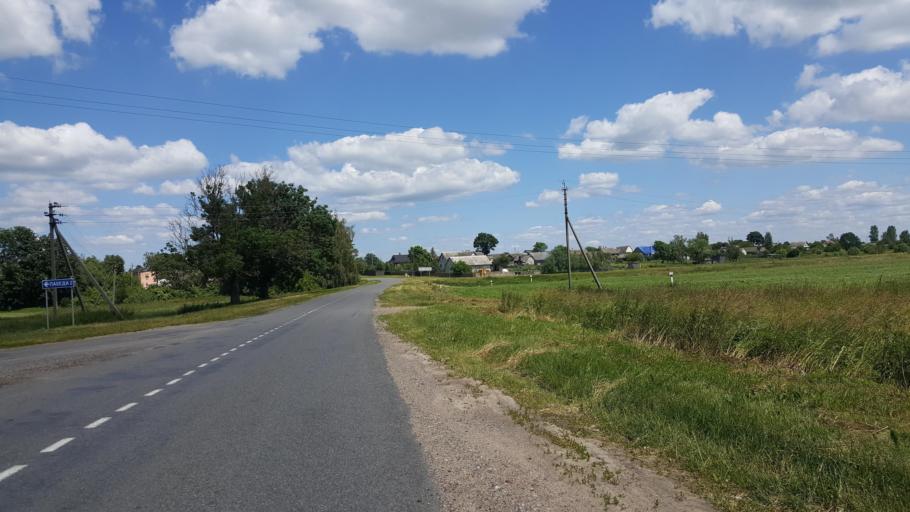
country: PL
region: Podlasie
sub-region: Powiat hajnowski
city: Czeremcha
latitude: 52.4660
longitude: 23.5075
